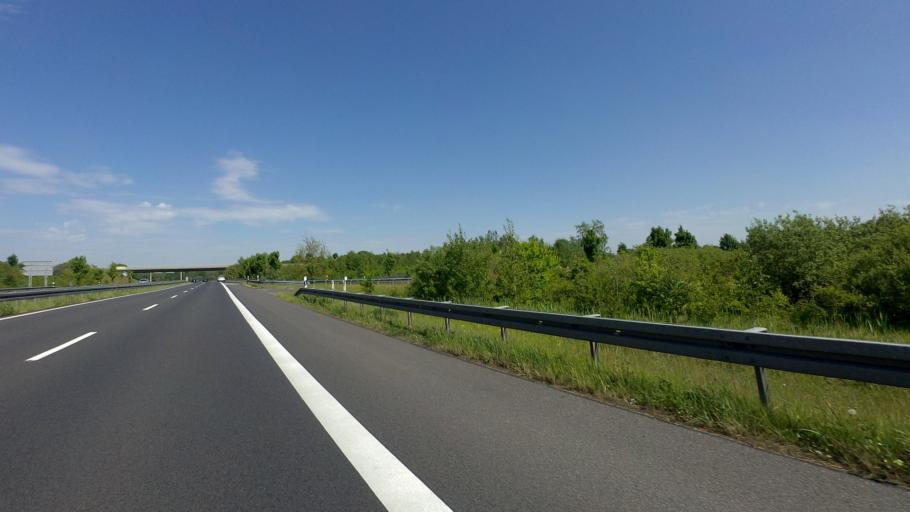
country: DE
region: Brandenburg
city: Leegebruch
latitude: 52.7378
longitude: 13.2085
